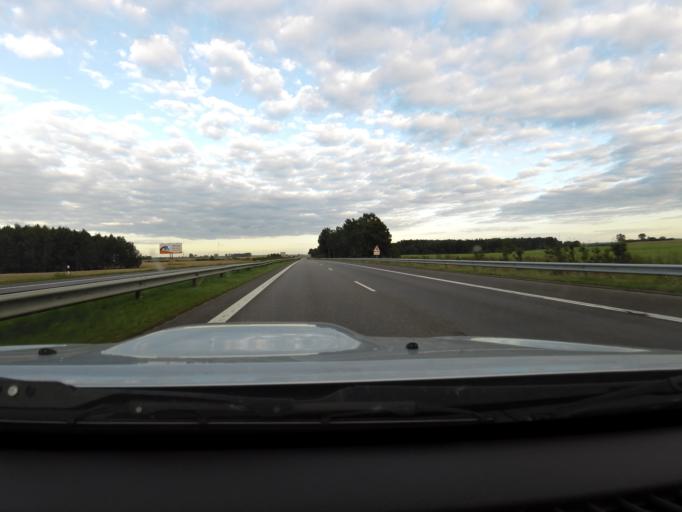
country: LT
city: Kaisiadorys
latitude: 54.8525
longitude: 24.3028
